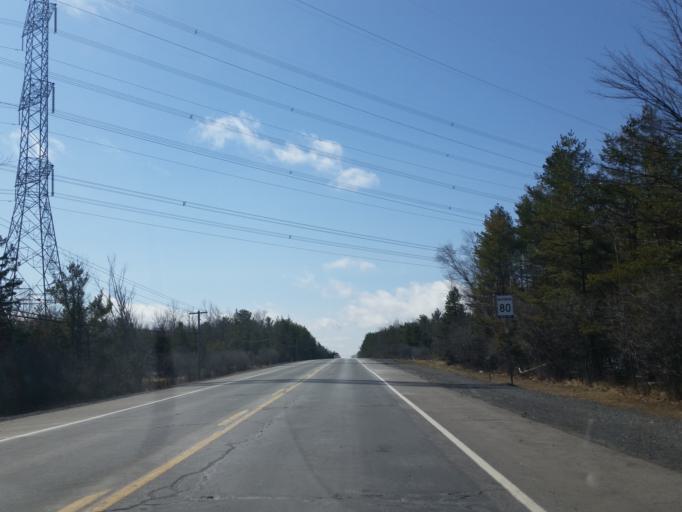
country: CA
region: Ontario
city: Bells Corners
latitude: 45.2959
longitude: -75.8343
